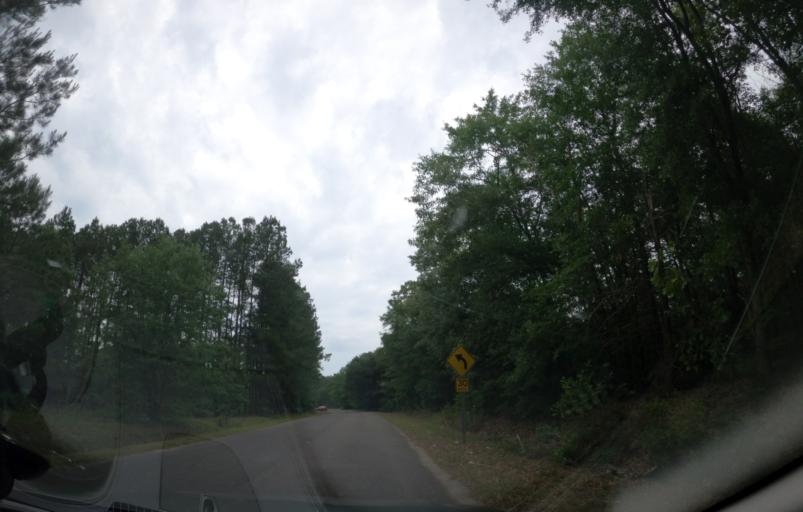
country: US
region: South Carolina
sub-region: Lexington County
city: Gaston
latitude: 33.6420
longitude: -81.2539
